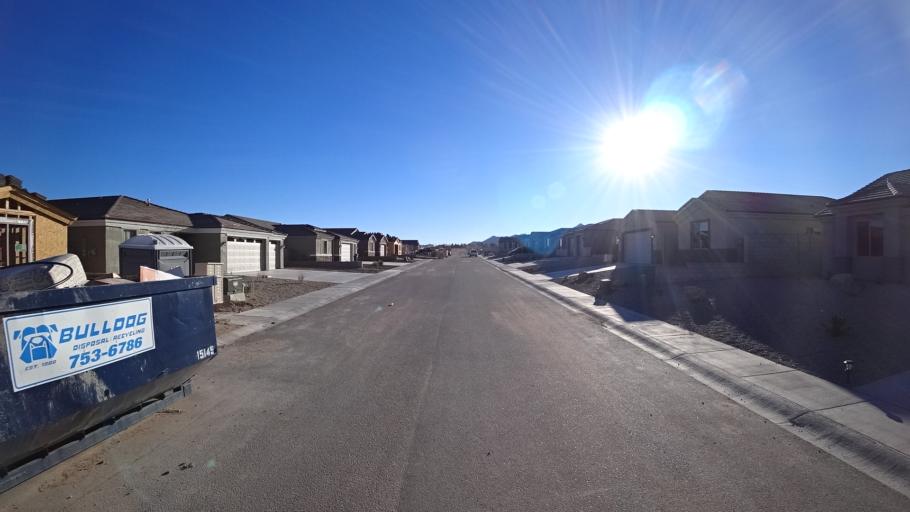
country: US
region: Arizona
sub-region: Mohave County
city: Kingman
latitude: 35.1908
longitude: -113.9998
